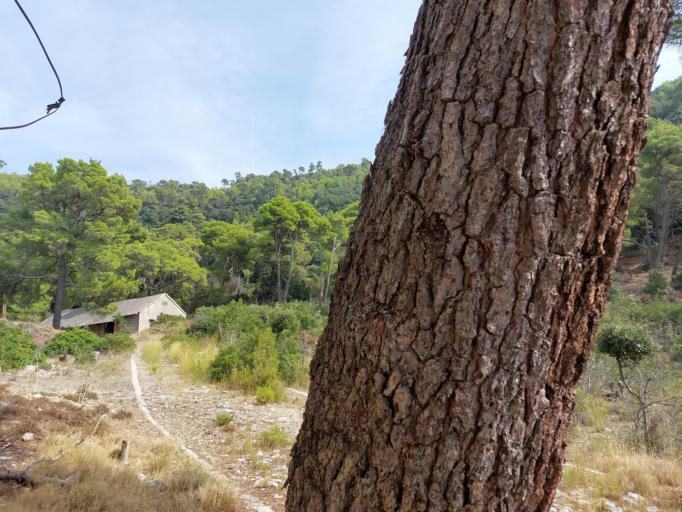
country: HR
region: Dubrovacko-Neretvanska
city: Smokvica
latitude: 42.7483
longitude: 16.8398
